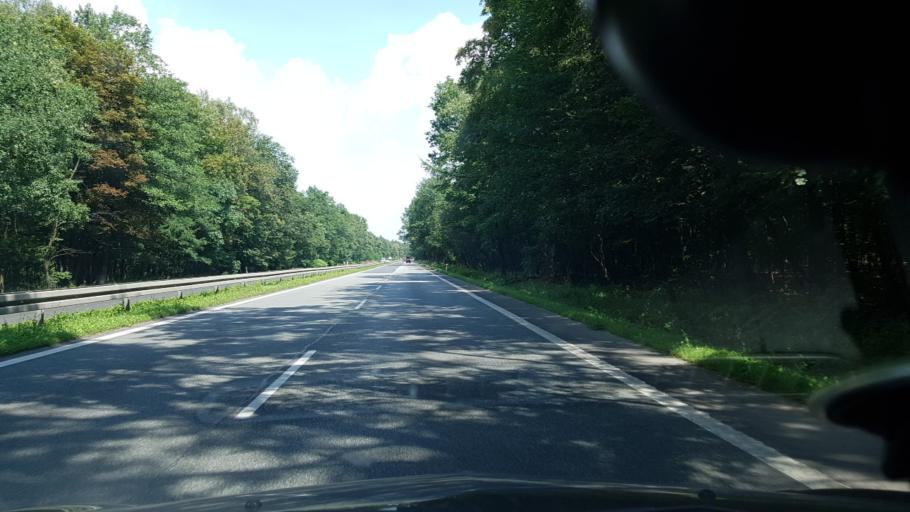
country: PL
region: Silesian Voivodeship
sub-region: Powiat mikolowski
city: Mikolow
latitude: 50.2005
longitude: 18.9412
